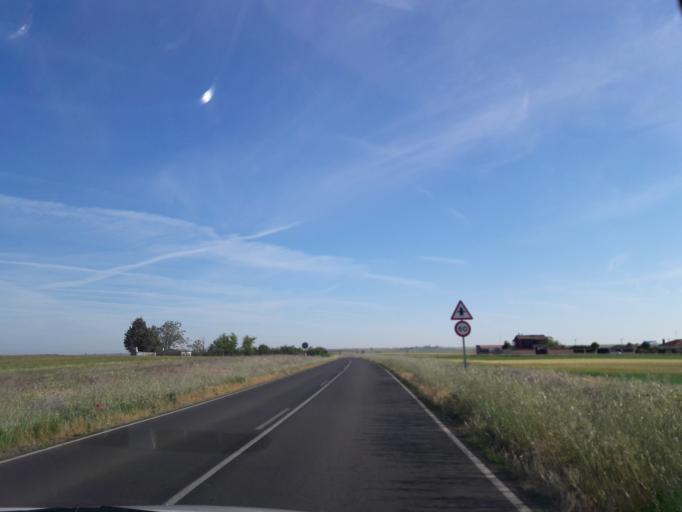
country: ES
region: Castille and Leon
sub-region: Provincia de Salamanca
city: Monterrubio de Armuna
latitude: 41.0252
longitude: -5.6507
